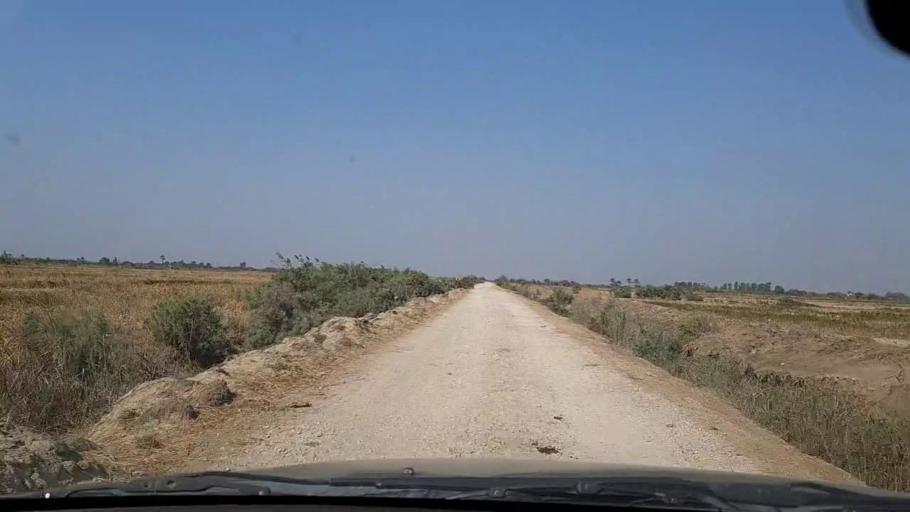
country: PK
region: Sindh
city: Mirpur Sakro
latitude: 24.3700
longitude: 67.6830
